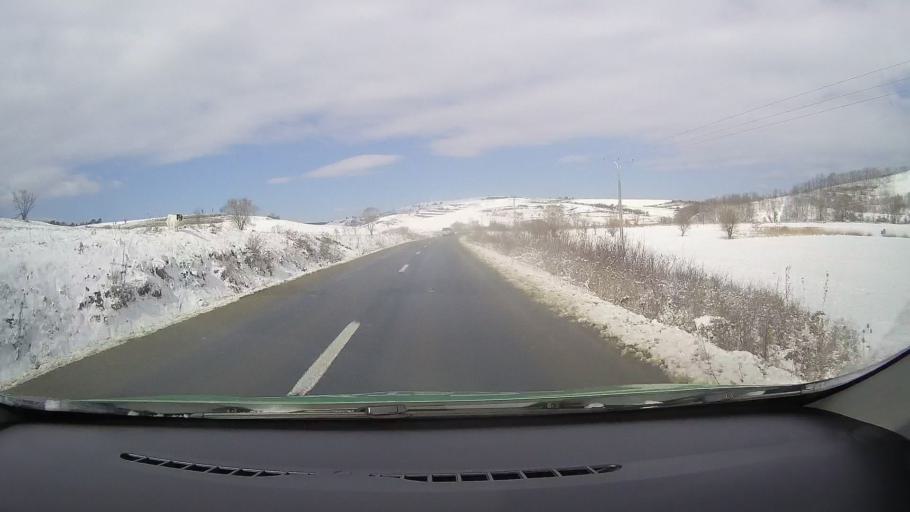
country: RO
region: Sibiu
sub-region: Comuna Altina
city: Altina
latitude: 45.9719
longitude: 24.4665
